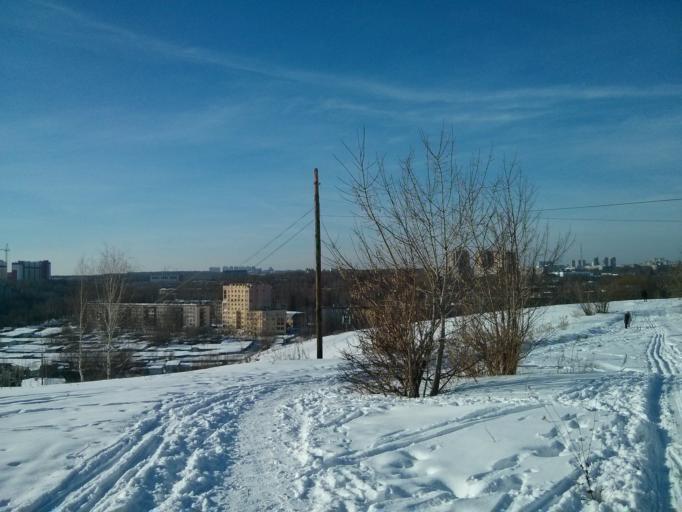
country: RU
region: Nizjnij Novgorod
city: Afonino
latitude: 56.2923
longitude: 44.0603
